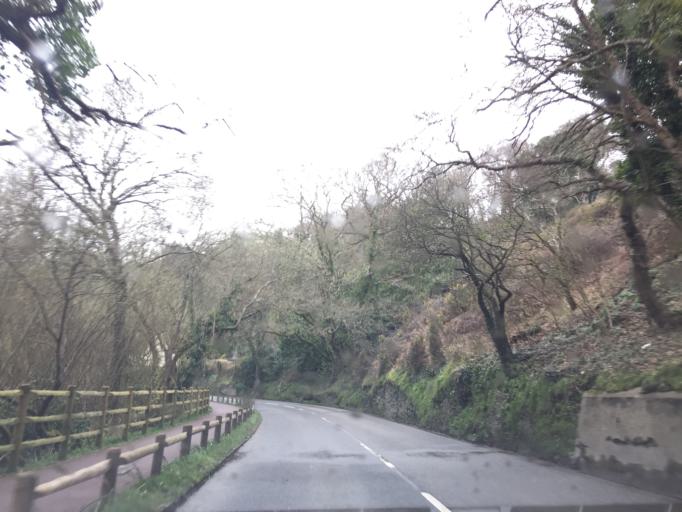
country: JE
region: St Helier
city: Saint Helier
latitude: 49.2077
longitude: -2.1581
